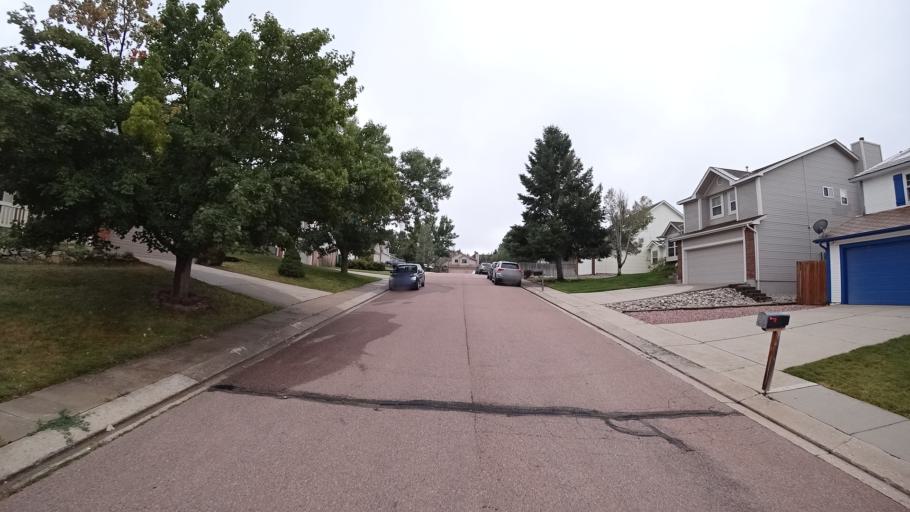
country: US
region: Colorado
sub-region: El Paso County
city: Cimarron Hills
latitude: 38.9238
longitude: -104.7571
